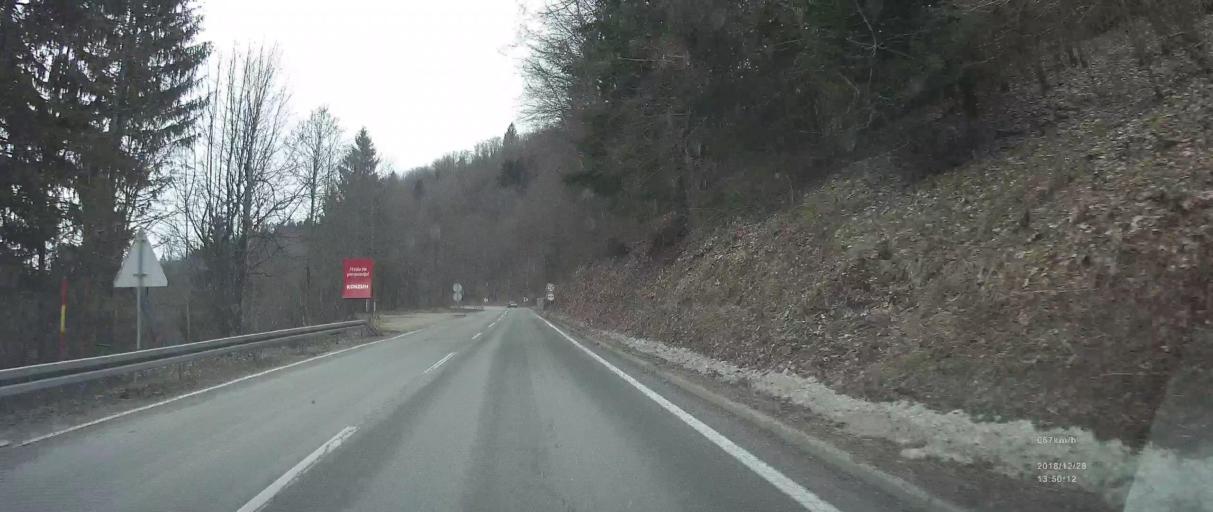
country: HR
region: Primorsko-Goranska
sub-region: Grad Delnice
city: Delnice
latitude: 45.3955
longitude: 14.8274
